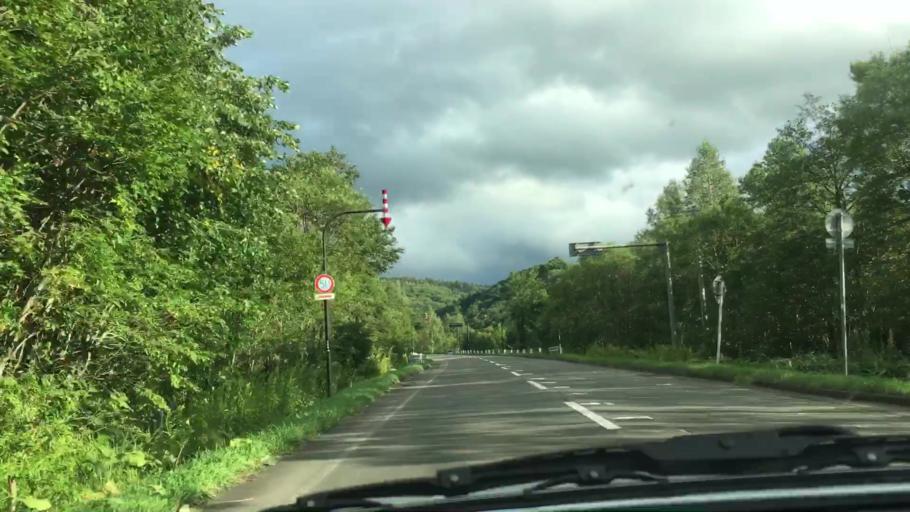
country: JP
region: Hokkaido
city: Shimo-furano
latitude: 43.1127
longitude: 142.6890
